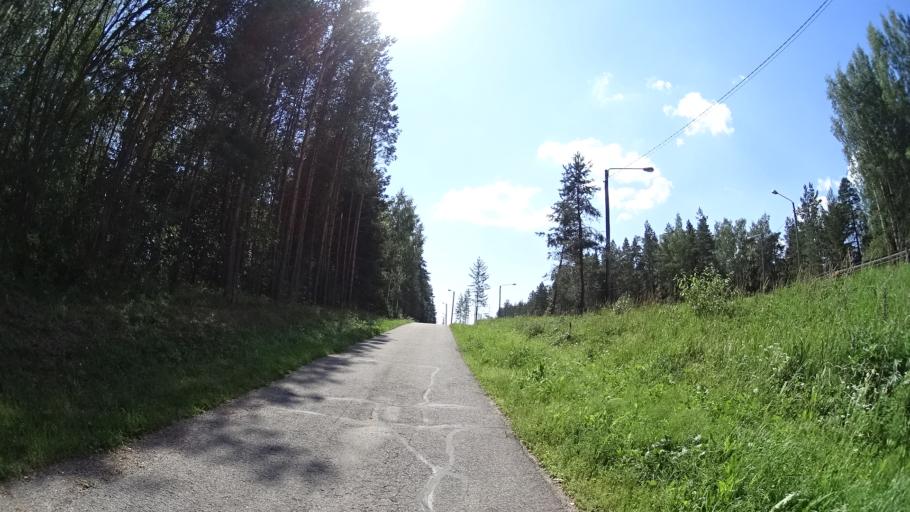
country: FI
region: Uusimaa
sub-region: Helsinki
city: Vantaa
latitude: 60.3190
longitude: 25.0007
